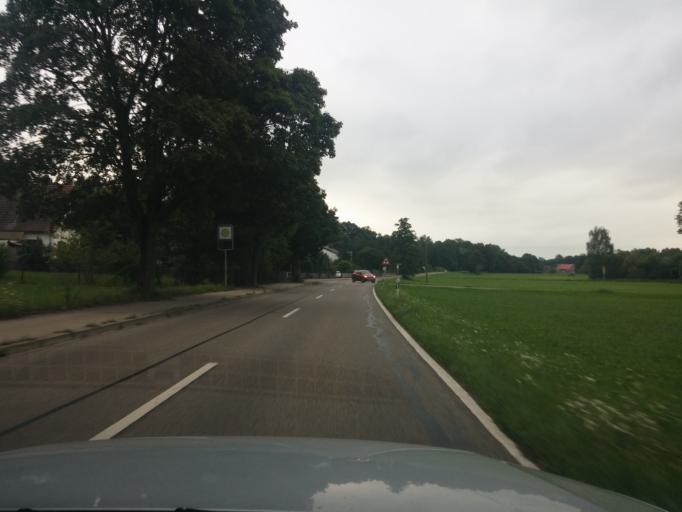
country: DE
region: Bavaria
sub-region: Swabia
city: Buxheim
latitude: 47.9856
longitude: 10.1442
